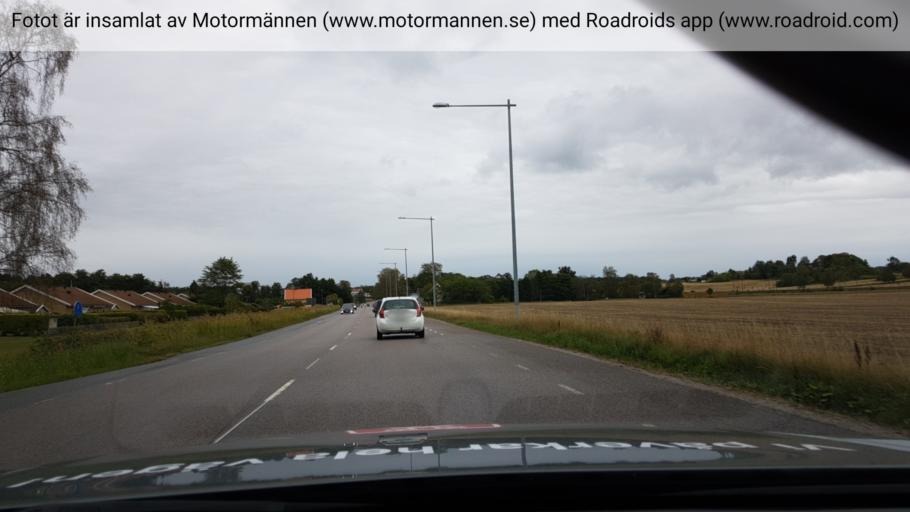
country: SE
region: Soedermanland
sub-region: Trosa Kommun
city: Vagnharad
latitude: 58.9404
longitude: 17.4780
